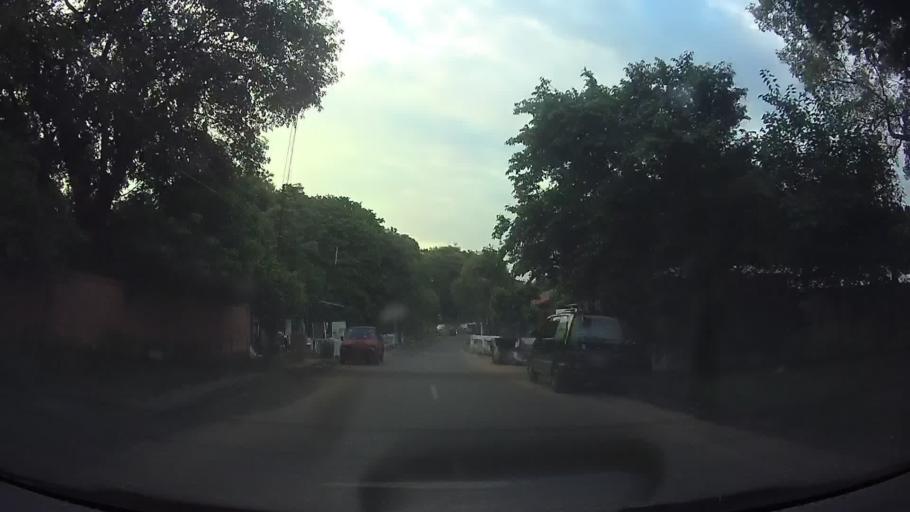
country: PY
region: Central
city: San Lorenzo
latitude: -25.2612
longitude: -57.4951
